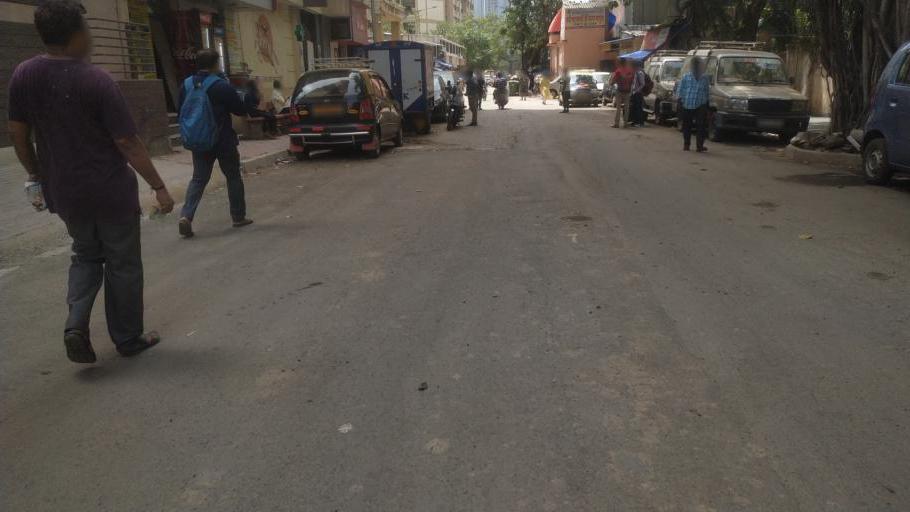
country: IN
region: Maharashtra
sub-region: Mumbai Suburban
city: Mumbai
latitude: 19.0004
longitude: 72.8258
